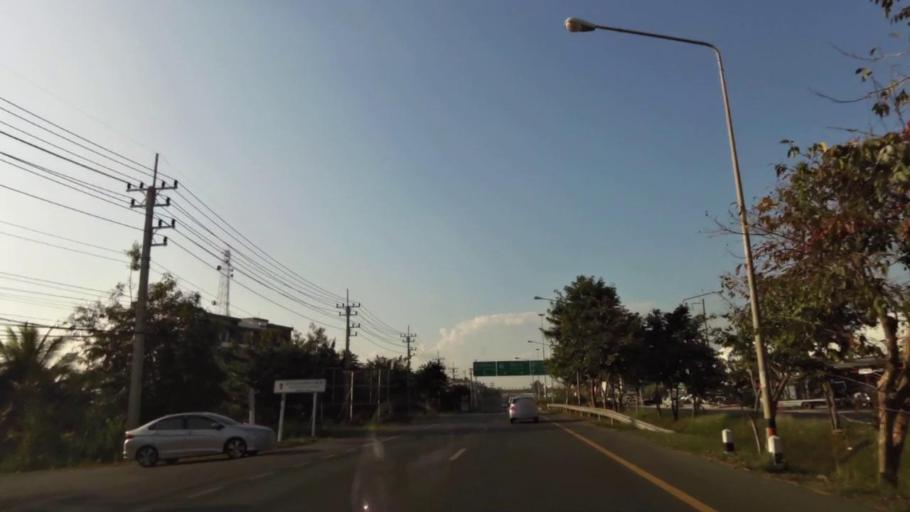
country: TH
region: Phayao
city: Phayao
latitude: 19.1691
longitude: 99.9081
